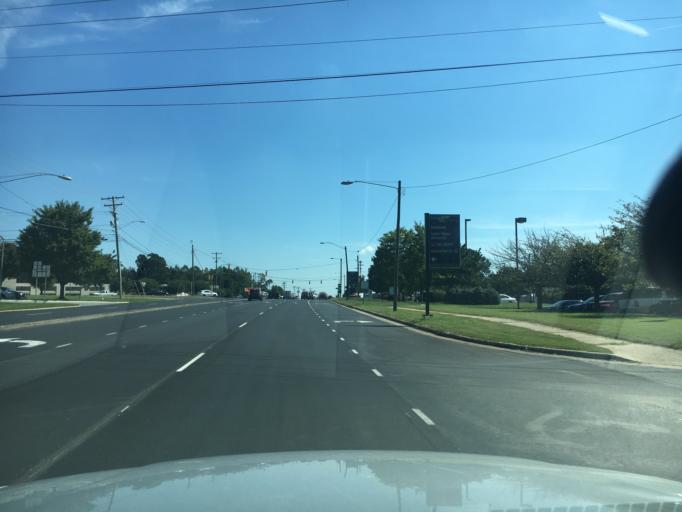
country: US
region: North Carolina
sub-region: Catawba County
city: Hickory
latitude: 35.7097
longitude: -81.3133
